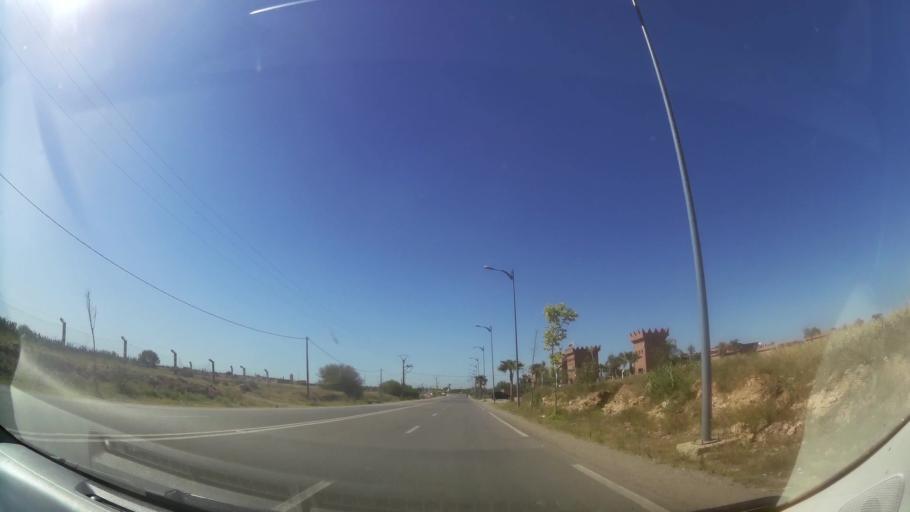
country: MA
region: Oriental
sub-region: Oujda-Angad
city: Oujda
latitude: 34.7166
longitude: -1.8641
